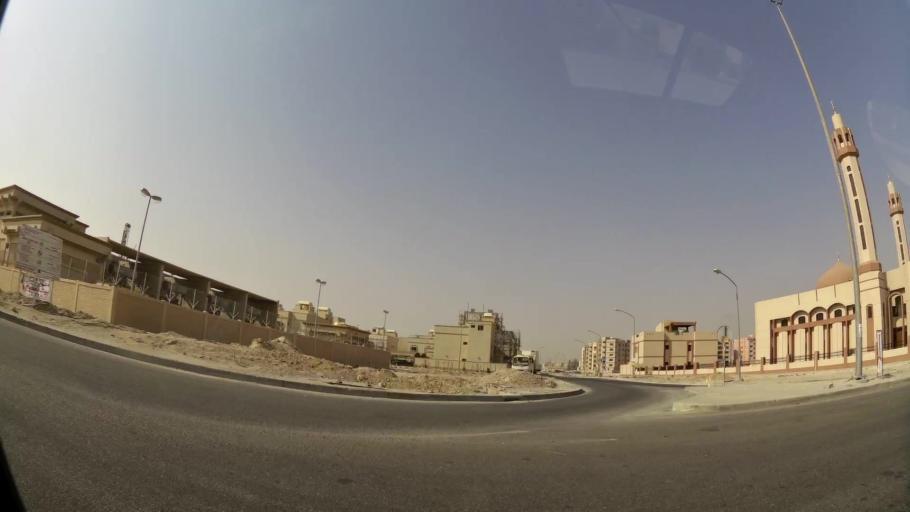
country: KW
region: Muhafazat al Jahra'
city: Al Jahra'
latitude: 29.3514
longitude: 47.7576
